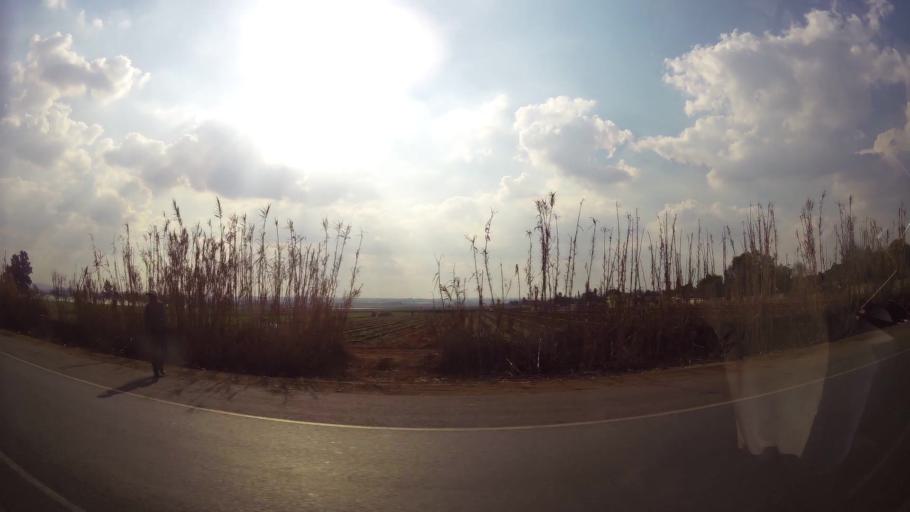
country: ZA
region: Gauteng
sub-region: Ekurhuleni Metropolitan Municipality
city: Germiston
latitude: -26.2940
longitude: 28.2137
